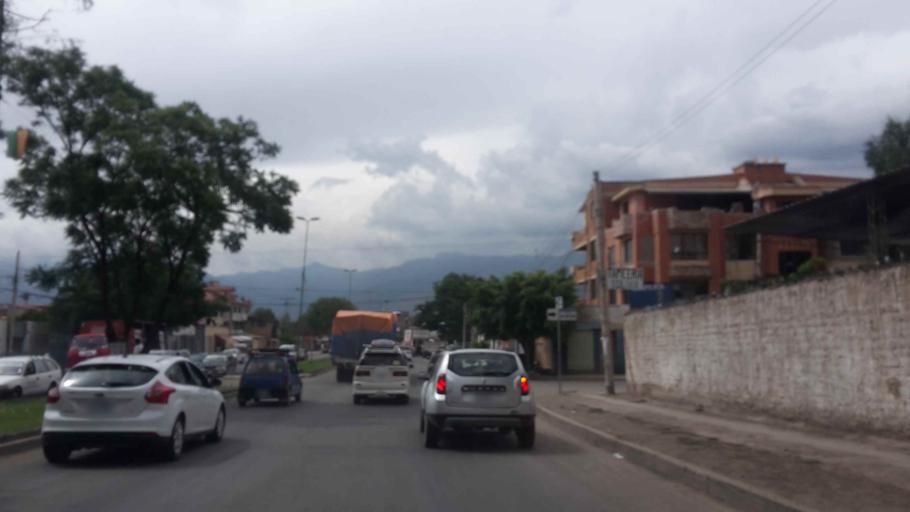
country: BO
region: Cochabamba
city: Cochabamba
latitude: -17.4080
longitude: -66.1760
